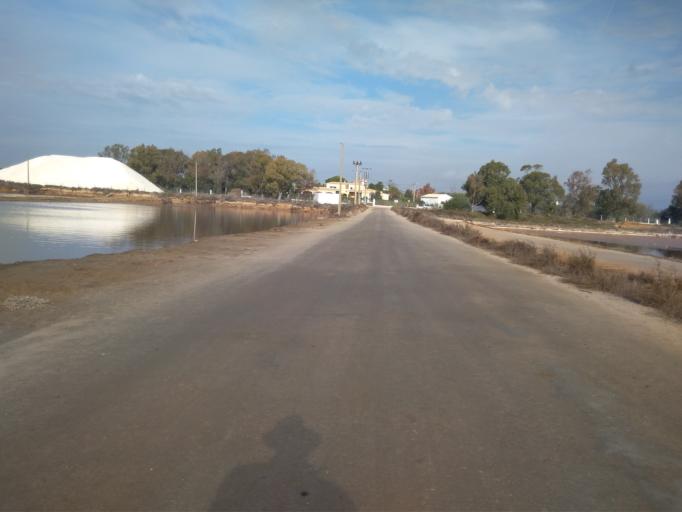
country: PT
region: Faro
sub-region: Faro
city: Faro
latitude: 37.0293
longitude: -7.9972
